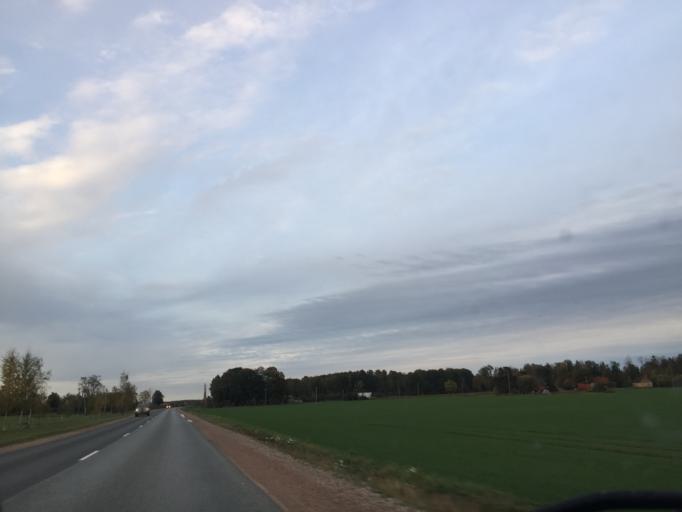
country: LV
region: Dobeles Rajons
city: Dobele
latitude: 56.7219
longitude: 23.3862
